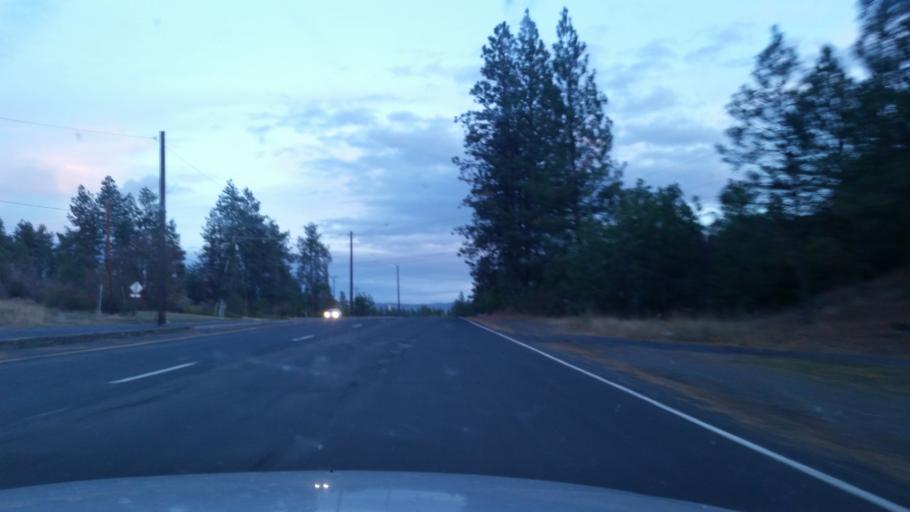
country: US
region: Washington
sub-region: Spokane County
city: Spokane
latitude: 47.6415
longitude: -117.4805
